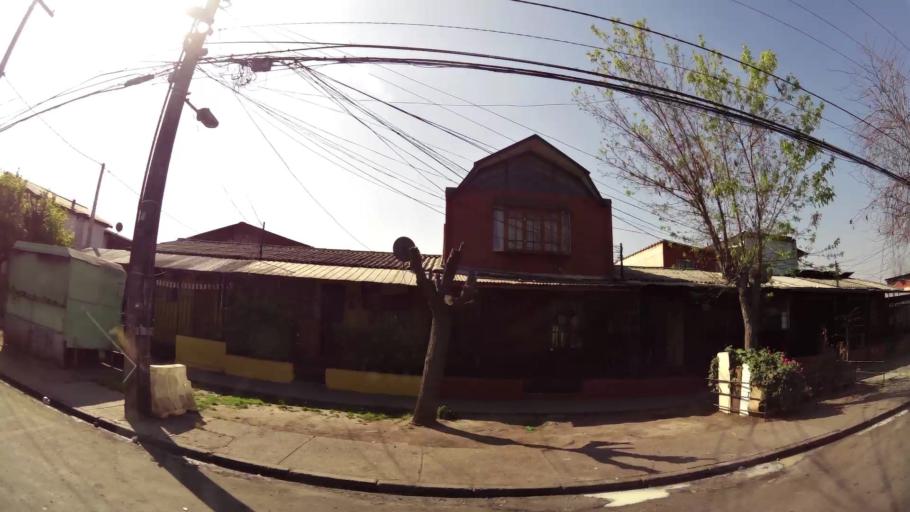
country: CL
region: Santiago Metropolitan
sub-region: Provincia de Santiago
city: Santiago
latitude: -33.4709
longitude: -70.6174
